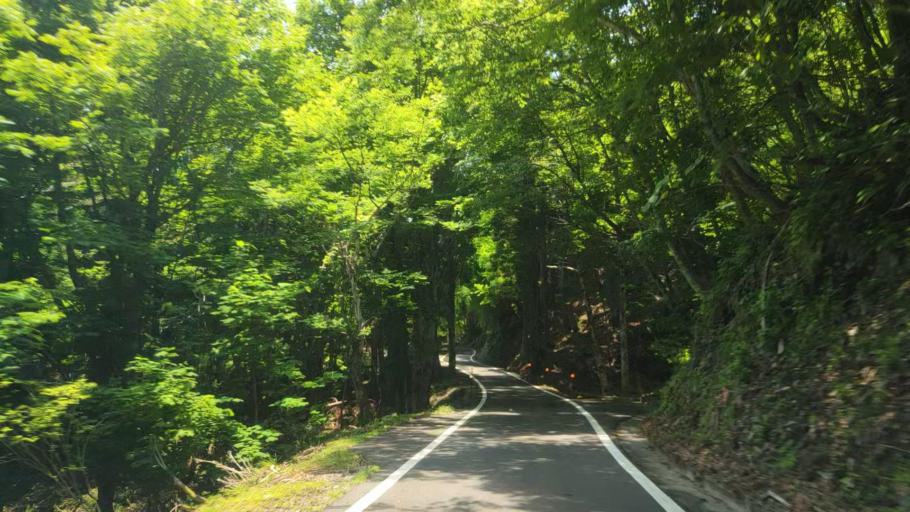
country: JP
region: Tottori
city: Tottori
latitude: 35.3759
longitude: 134.4903
